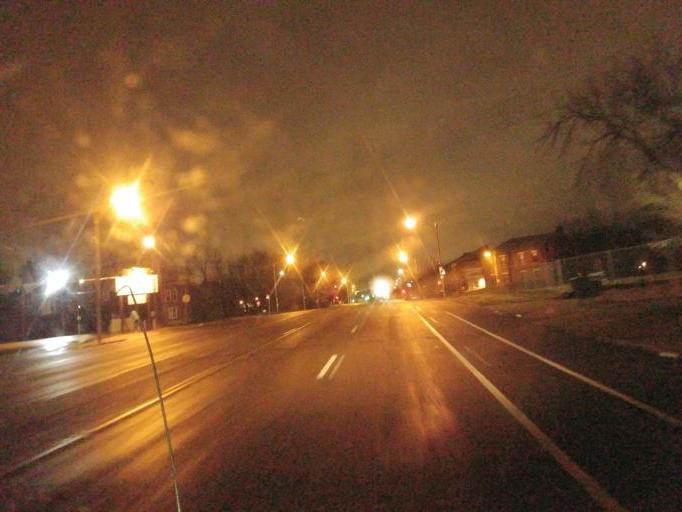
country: US
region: Missouri
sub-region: City of Saint Louis
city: St. Louis
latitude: 38.6530
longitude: -90.2012
